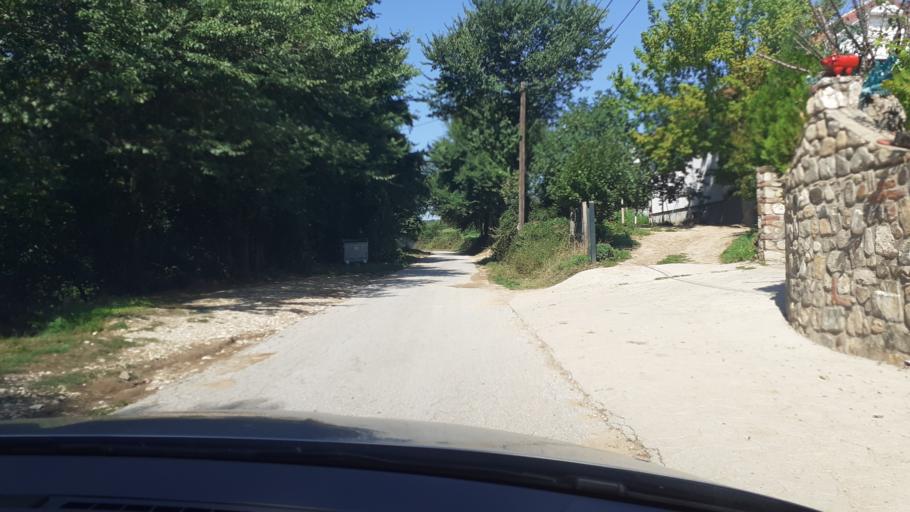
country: MK
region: Strumica
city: Veljusa
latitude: 41.5189
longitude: 22.6043
